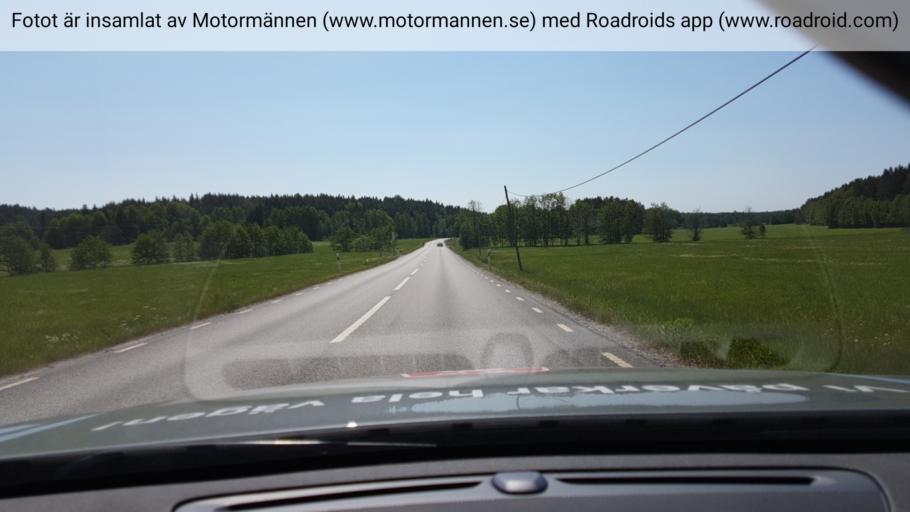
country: SE
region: Stockholm
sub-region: Norrtalje Kommun
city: Rimbo
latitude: 59.6593
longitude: 18.3409
